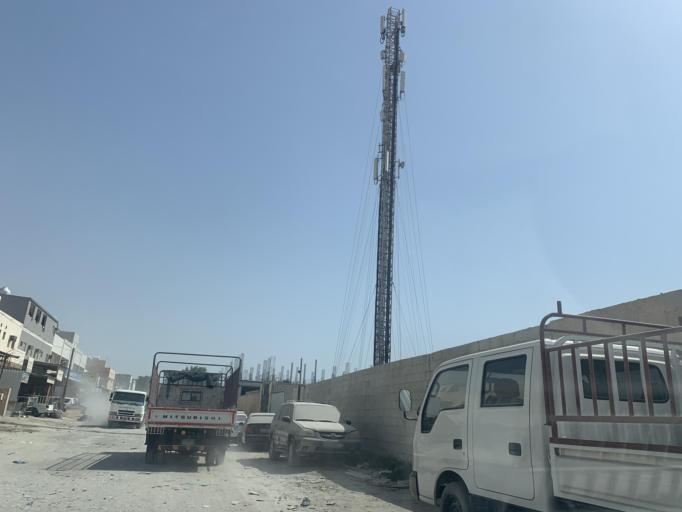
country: BH
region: Central Governorate
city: Madinat Hamad
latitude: 26.1392
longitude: 50.4837
